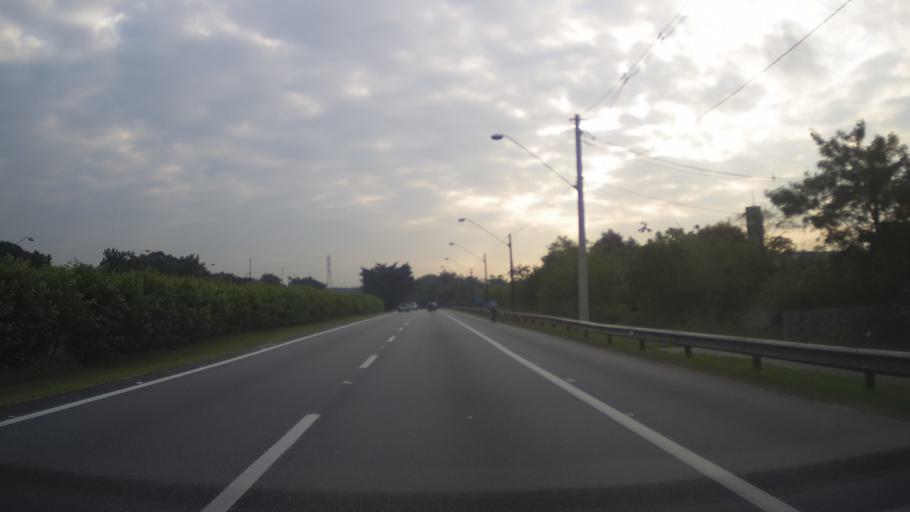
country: BR
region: Sao Paulo
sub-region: Cubatao
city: Cubatao
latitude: -23.9220
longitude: -46.4207
